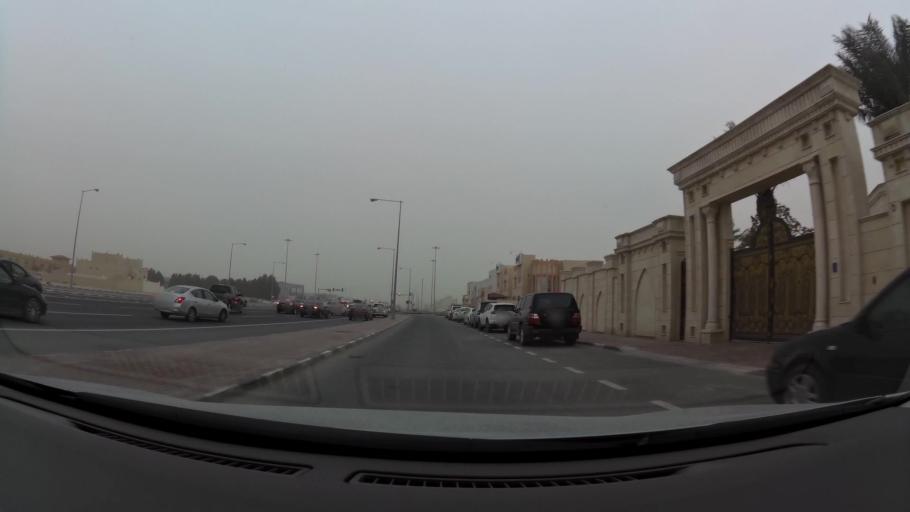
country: QA
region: Baladiyat ad Dawhah
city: Doha
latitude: 25.2395
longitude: 51.4967
